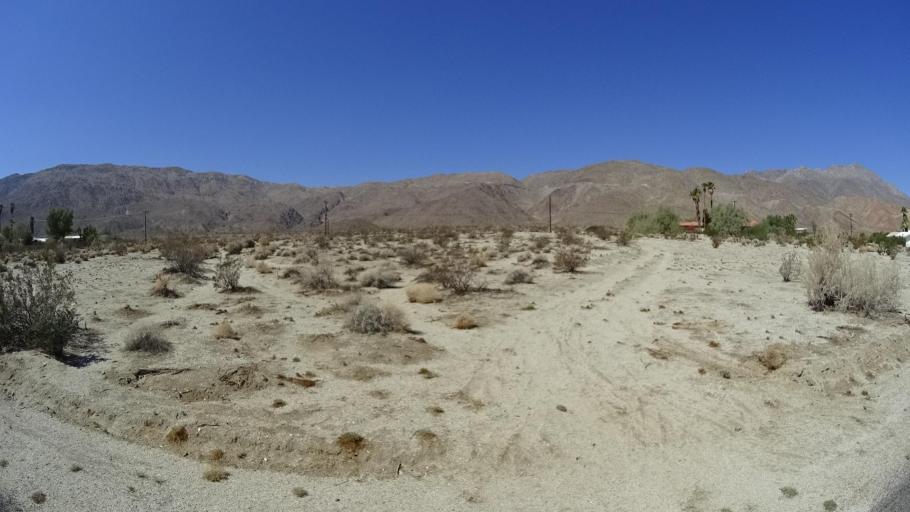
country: US
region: California
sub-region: San Diego County
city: Borrego Springs
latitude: 33.2251
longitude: -116.3920
